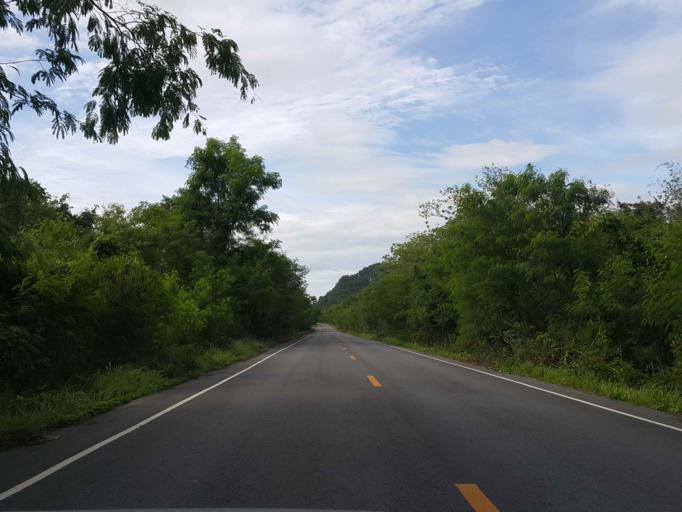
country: TH
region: Sukhothai
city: Thung Saliam
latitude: 17.2937
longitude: 99.5269
